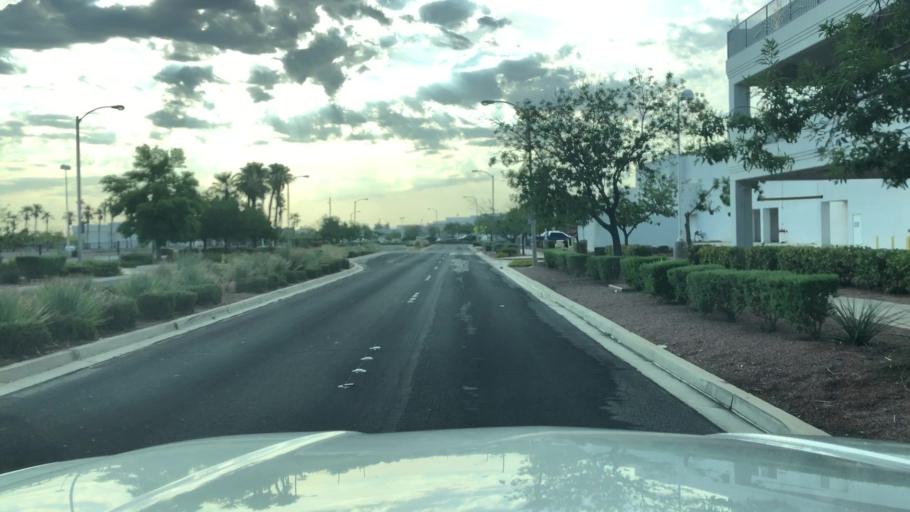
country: US
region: Nevada
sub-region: Clark County
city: Whitney
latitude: 36.0727
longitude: -115.0773
